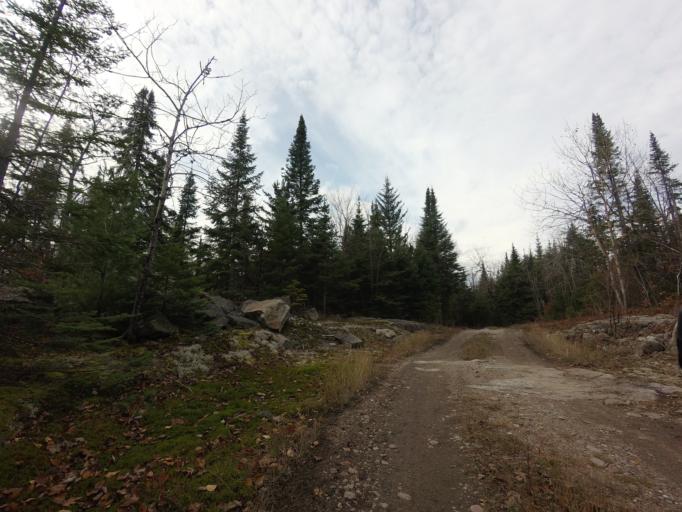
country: CA
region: Quebec
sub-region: Outaouais
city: Wakefield
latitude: 45.5425
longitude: -75.9600
